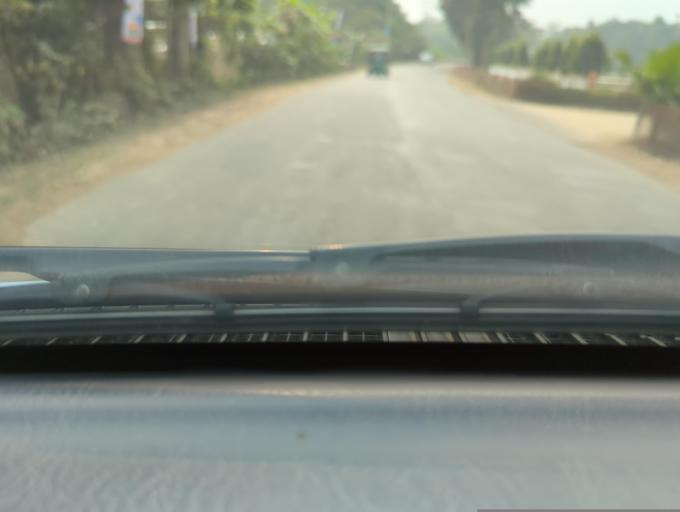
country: BD
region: Sylhet
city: Maulavi Bazar
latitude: 24.5273
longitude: 91.7338
